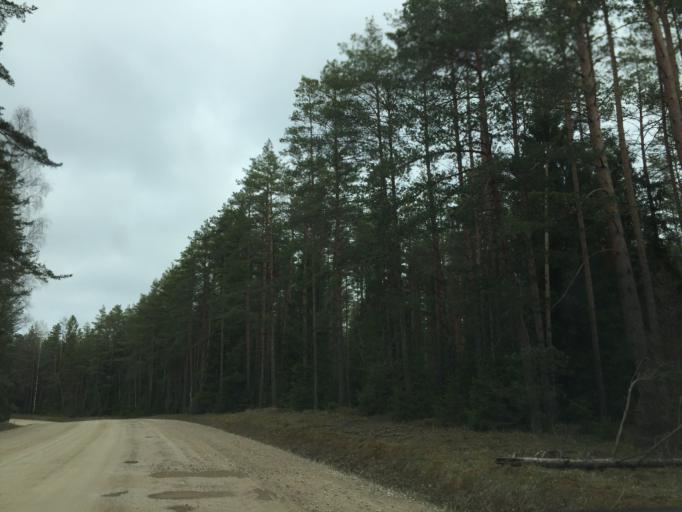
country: EE
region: Valgamaa
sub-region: Valga linn
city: Valga
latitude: 57.5908
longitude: 26.2204
